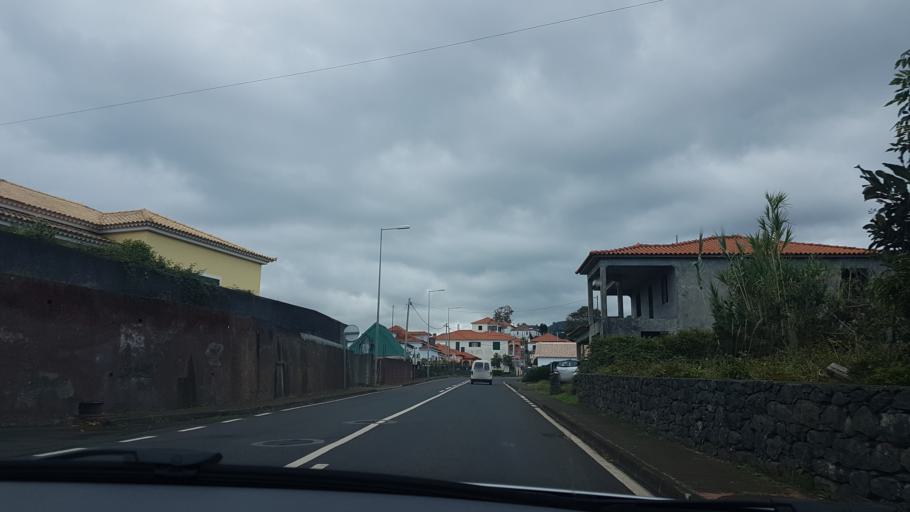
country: PT
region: Madeira
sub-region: Santana
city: Santana
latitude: 32.8179
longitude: -16.8872
